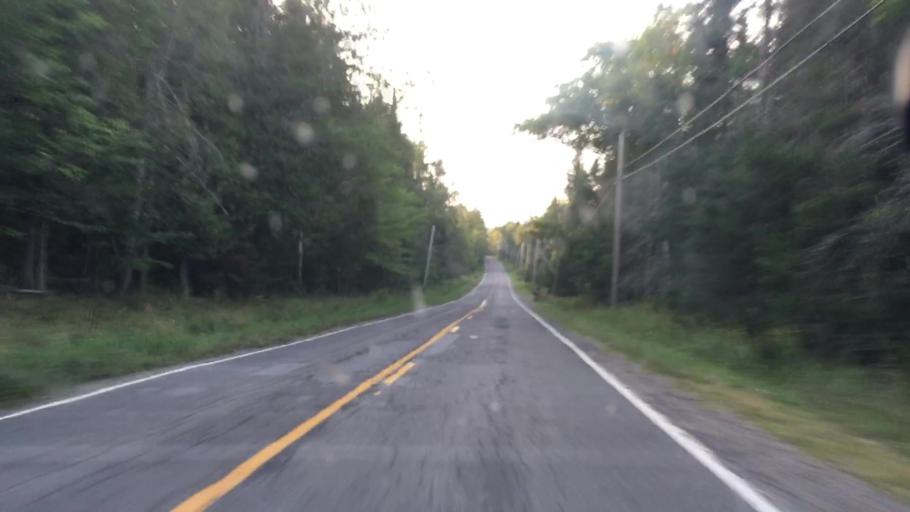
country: US
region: Maine
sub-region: Penobscot County
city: Hermon
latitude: 44.7028
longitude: -68.9469
